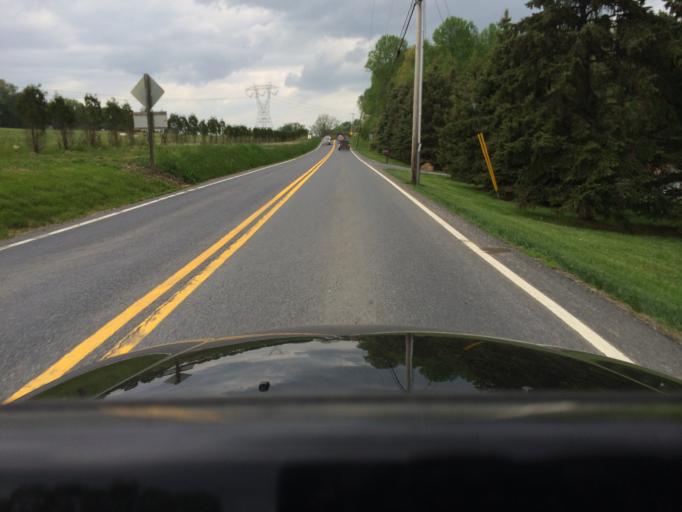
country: US
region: Maryland
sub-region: Carroll County
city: Eldersburg
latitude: 39.4235
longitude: -77.0098
